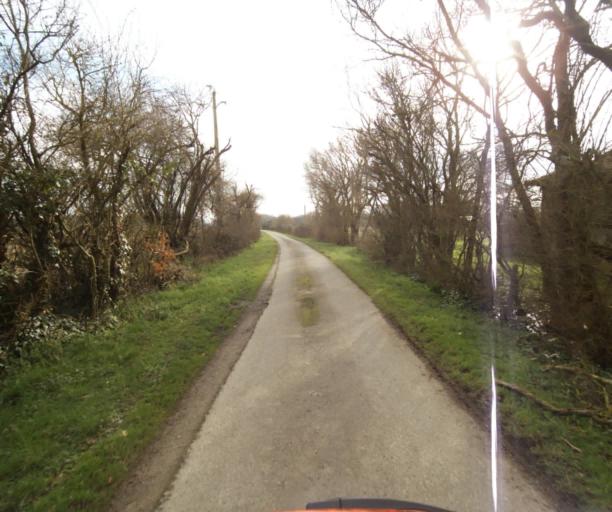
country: FR
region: Midi-Pyrenees
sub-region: Departement de l'Ariege
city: Mazeres
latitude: 43.2125
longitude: 1.6801
